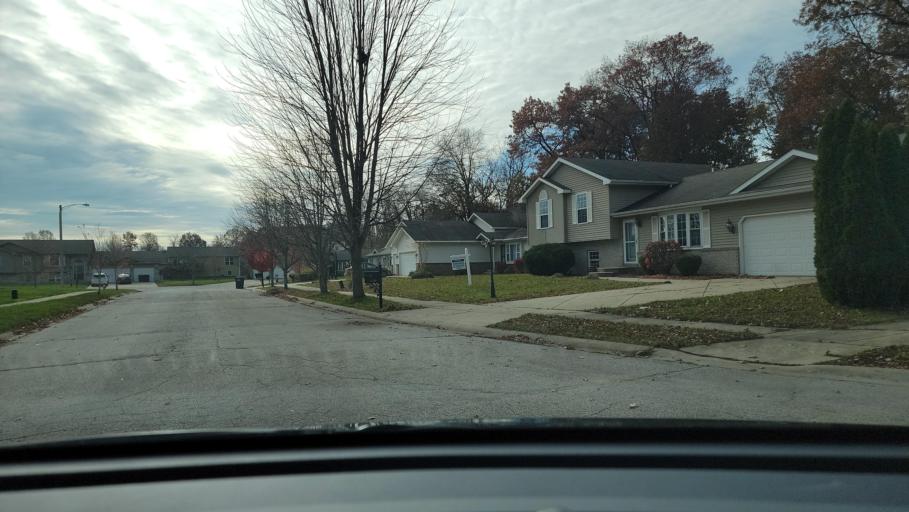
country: US
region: Indiana
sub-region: Porter County
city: Burns Harbor
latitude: 41.5839
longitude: -87.1289
